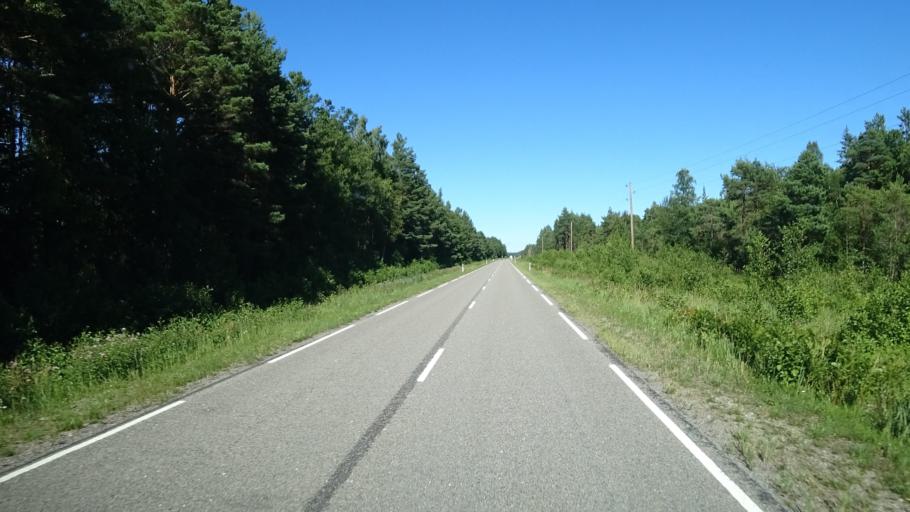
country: LV
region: Dundaga
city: Dundaga
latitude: 57.7073
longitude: 22.4382
